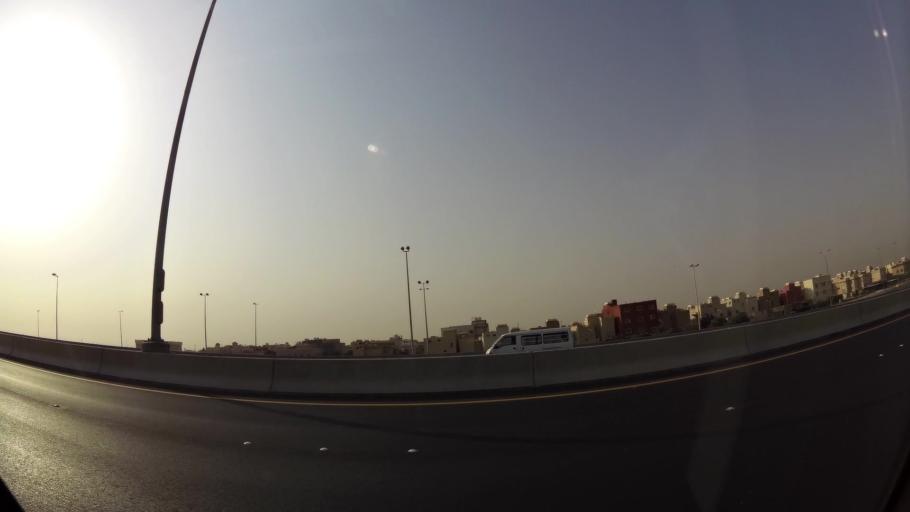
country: KW
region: Al Asimah
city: Ar Rabiyah
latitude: 29.3109
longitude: 47.8588
